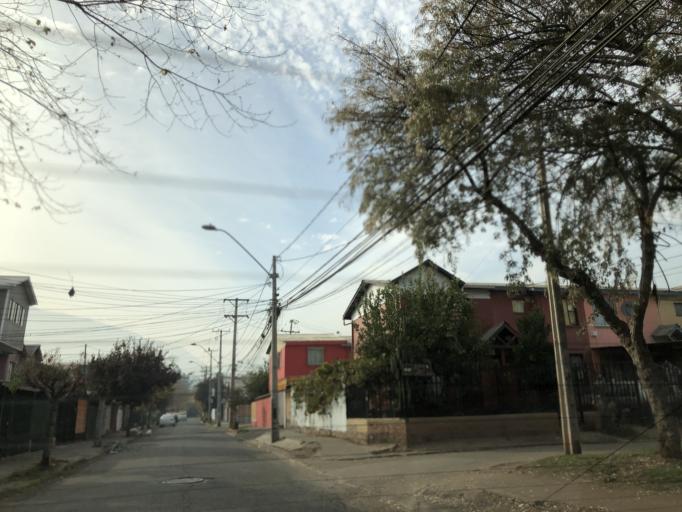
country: CL
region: Santiago Metropolitan
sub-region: Provincia de Cordillera
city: Puente Alto
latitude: -33.5800
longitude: -70.5554
